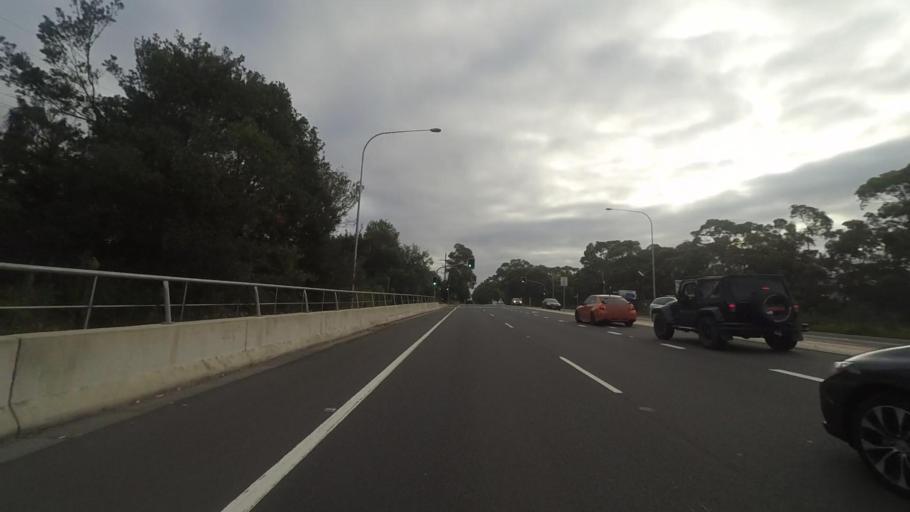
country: AU
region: New South Wales
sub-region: Sutherland Shire
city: Menai
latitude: -34.0353
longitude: 151.0032
